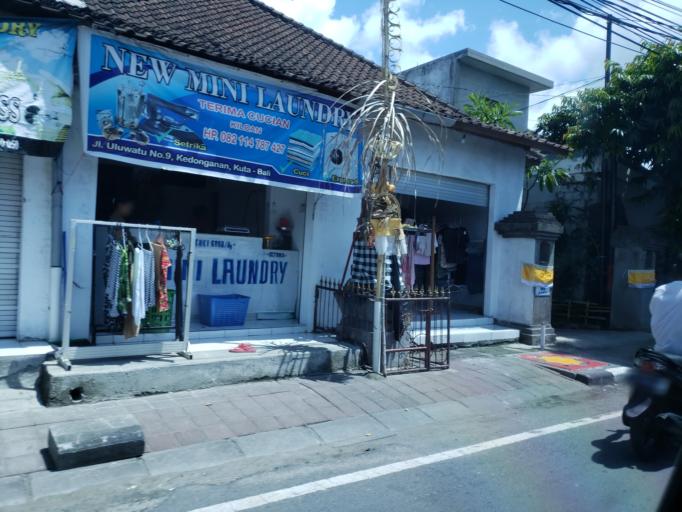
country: ID
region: Bali
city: Kelanabian
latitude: -8.7588
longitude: 115.1764
